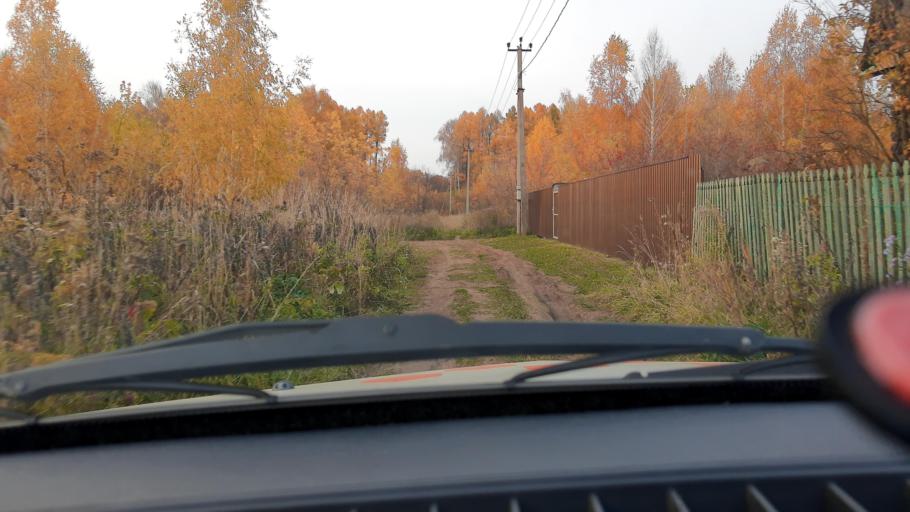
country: RU
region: Bashkortostan
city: Iglino
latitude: 54.8061
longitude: 56.3485
